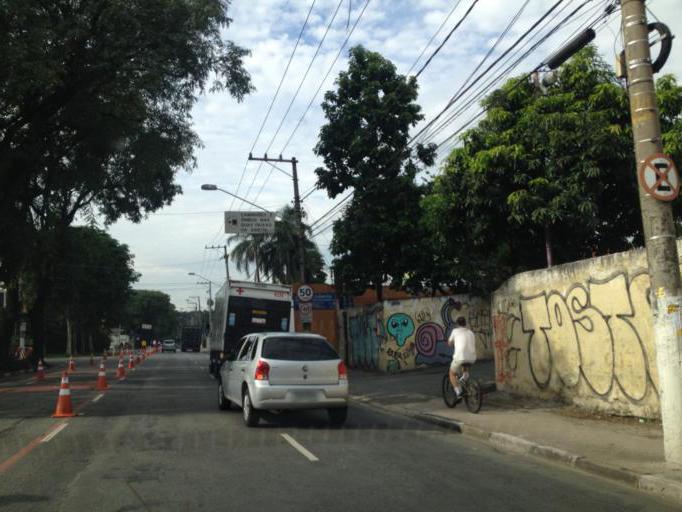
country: BR
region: Sao Paulo
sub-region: Sao Paulo
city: Sao Paulo
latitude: -23.5605
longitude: -46.7120
